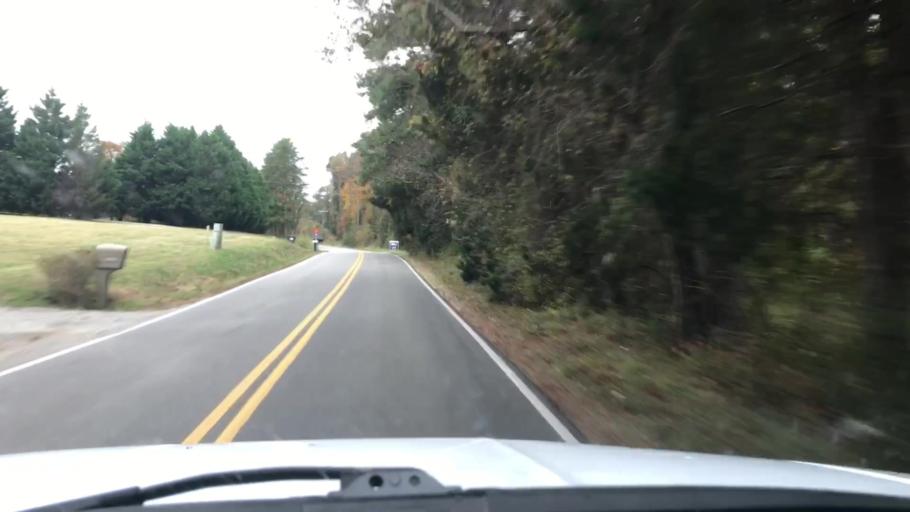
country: US
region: Virginia
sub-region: Goochland County
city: Goochland
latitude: 37.6748
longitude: -77.8767
